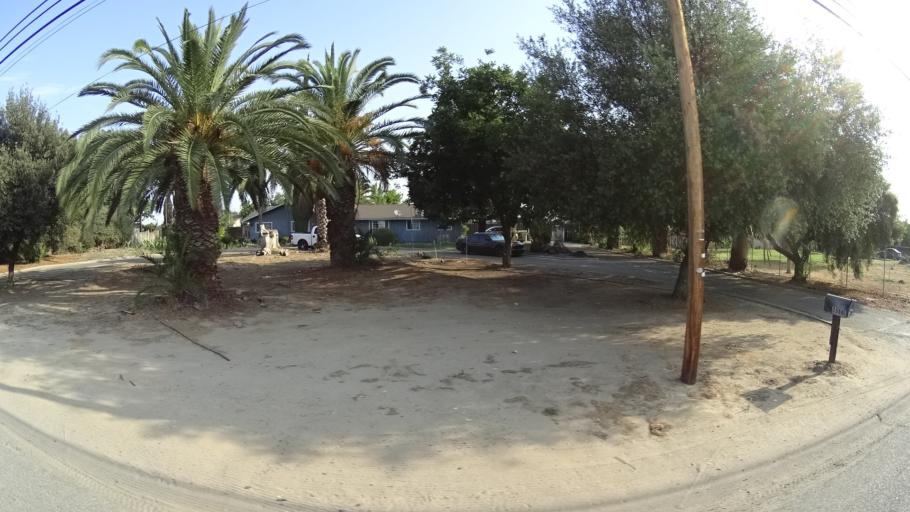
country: US
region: California
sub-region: Fresno County
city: West Park
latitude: 36.7501
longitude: -119.8572
